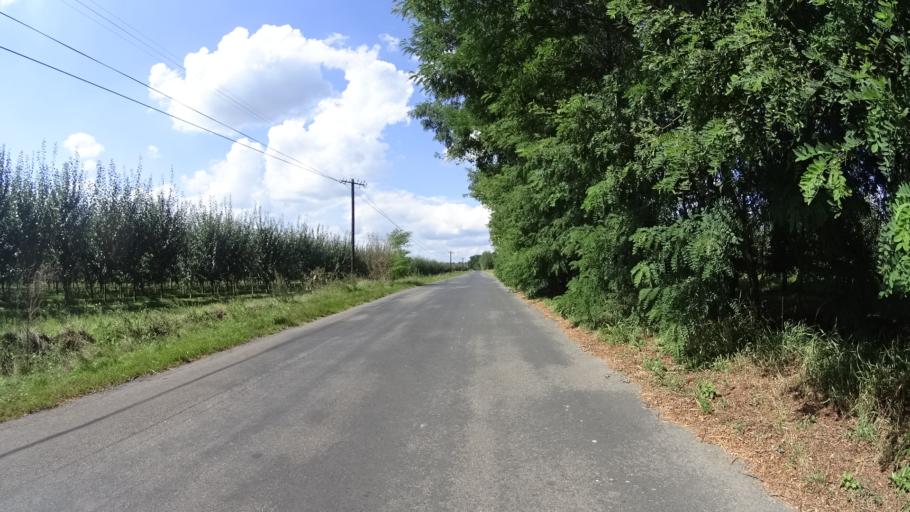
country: PL
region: Masovian Voivodeship
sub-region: Powiat grojecki
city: Mogielnica
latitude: 51.6873
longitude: 20.7529
